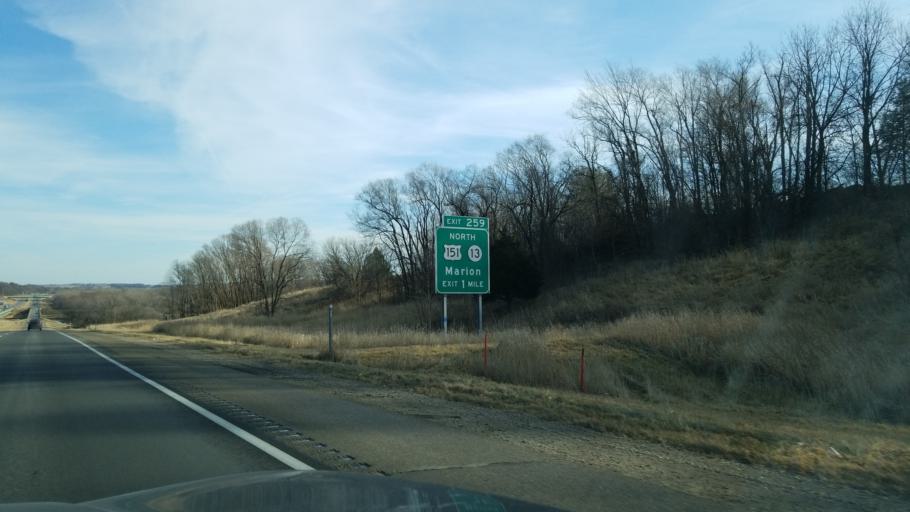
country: US
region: Iowa
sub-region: Linn County
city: Ely
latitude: 41.9254
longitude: -91.5609
